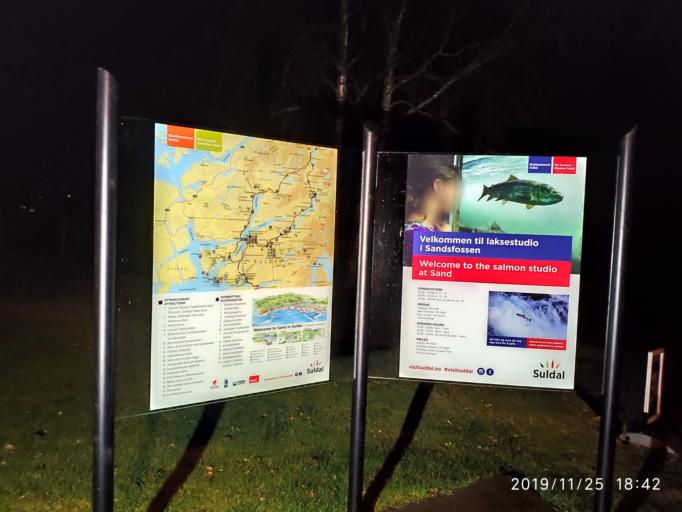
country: NO
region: Rogaland
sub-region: Suldal
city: Sand
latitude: 59.4817
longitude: 6.2566
